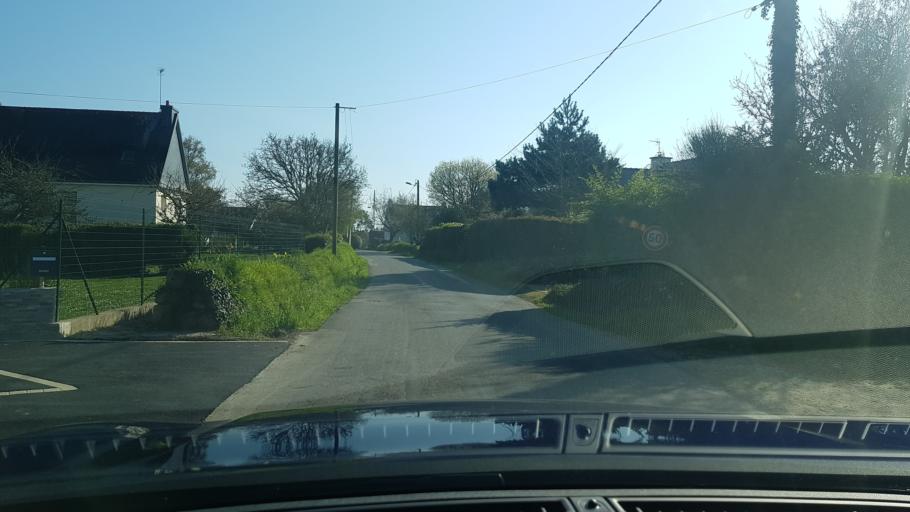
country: FR
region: Brittany
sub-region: Departement du Finistere
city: Moelan-sur-Mer
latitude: 47.7845
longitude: -3.6270
